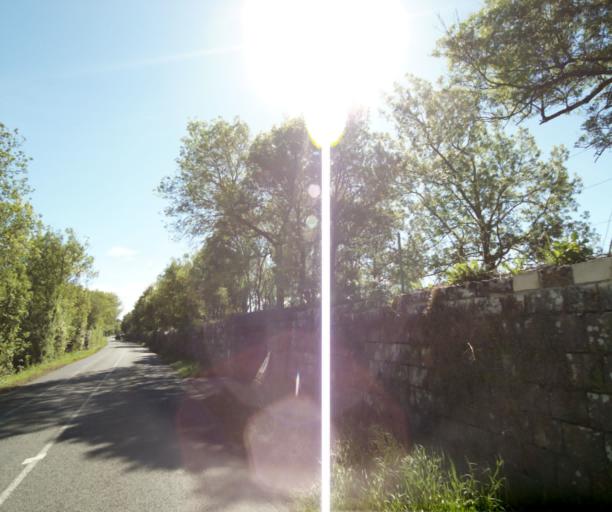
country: FR
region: Poitou-Charentes
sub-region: Departement de la Charente-Maritime
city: Bussac-sur-Charente
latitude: 45.8277
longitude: -0.6545
